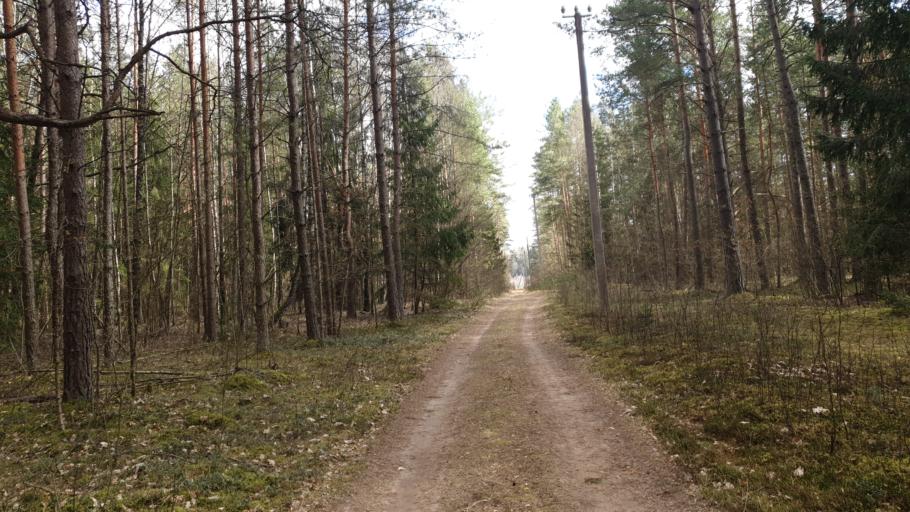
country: LT
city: Grigiskes
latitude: 54.7254
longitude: 25.0314
